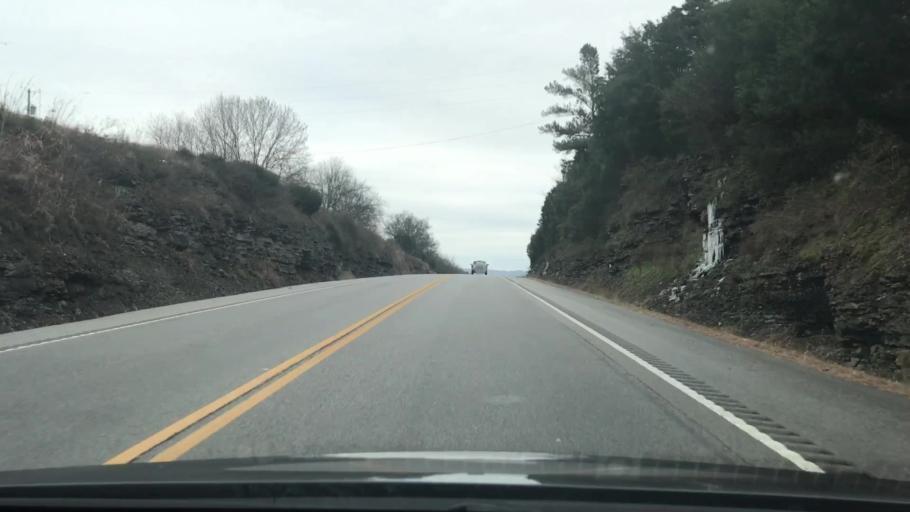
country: US
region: Tennessee
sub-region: Trousdale County
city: Hartsville
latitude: 36.3695
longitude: -86.0954
